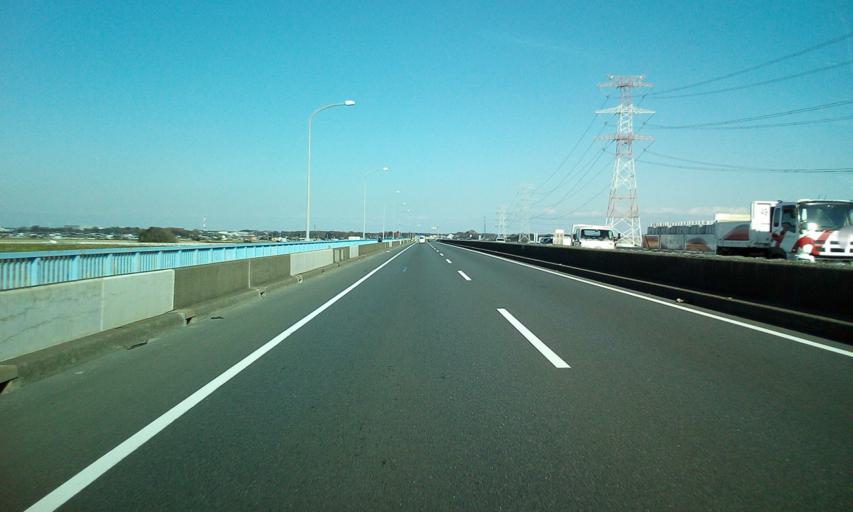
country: JP
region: Ibaraki
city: Sakai
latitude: 36.1267
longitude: 139.7582
